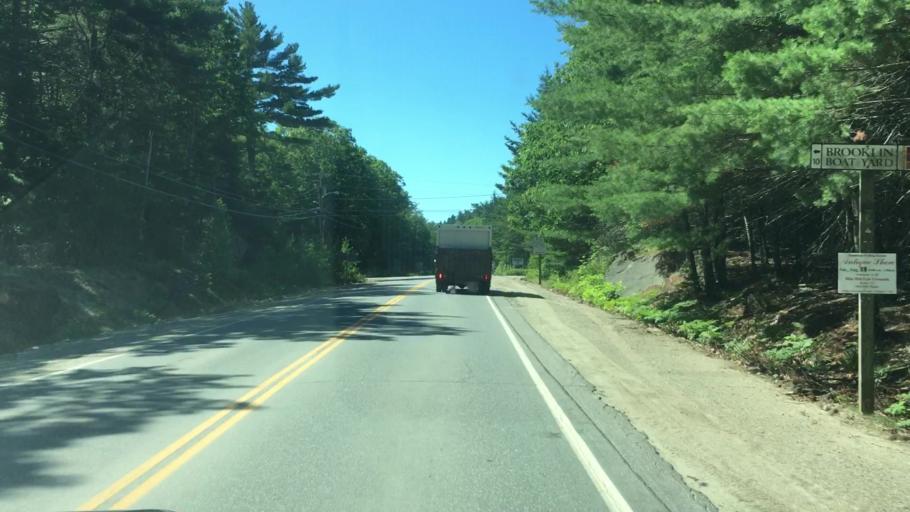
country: US
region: Maine
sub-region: Hancock County
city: Sedgwick
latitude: 44.3807
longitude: -68.5686
